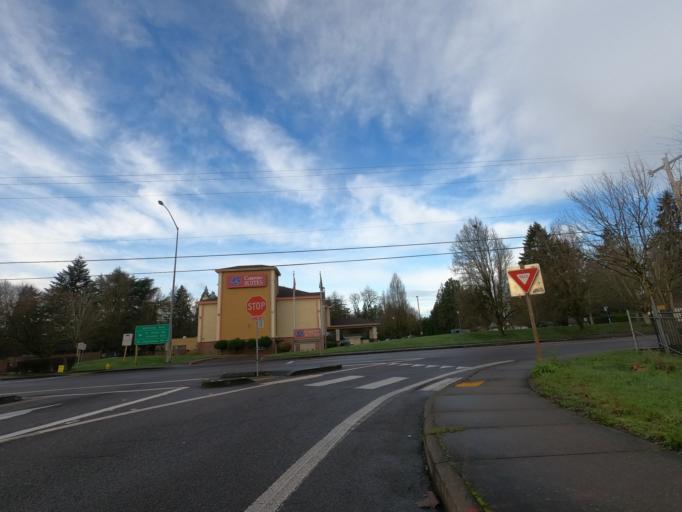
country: US
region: Oregon
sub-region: Clackamas County
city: Clackamas
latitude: 45.4076
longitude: -122.5729
